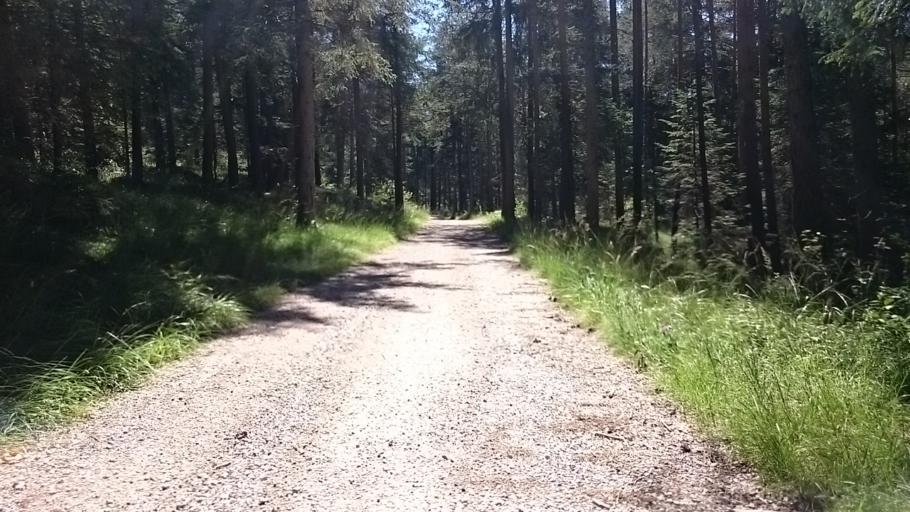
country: IT
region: Veneto
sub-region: Provincia di Belluno
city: San Vito
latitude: 46.4952
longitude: 12.1781
